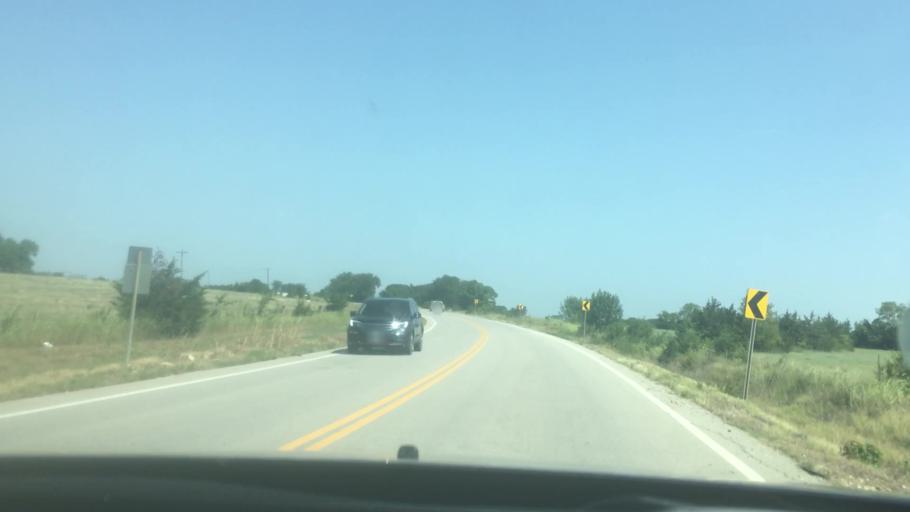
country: US
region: Oklahoma
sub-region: Bryan County
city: Durant
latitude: 34.1458
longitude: -96.3735
